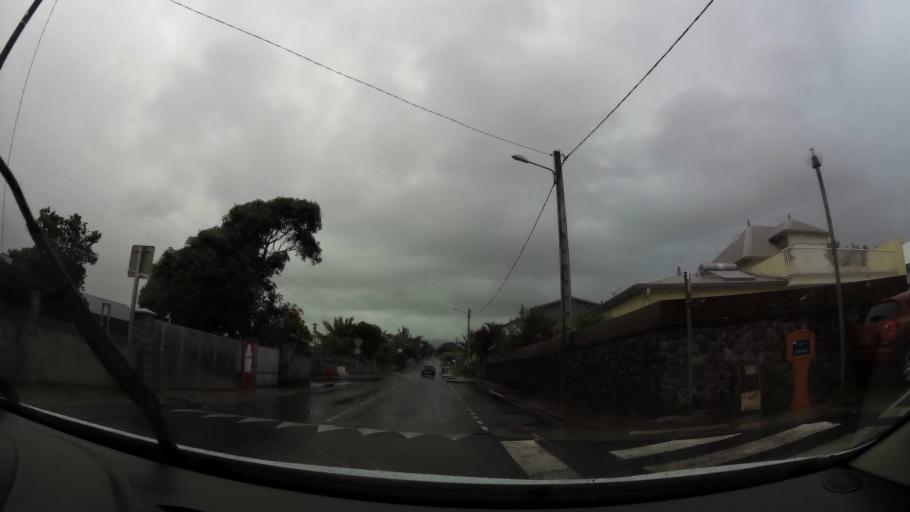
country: RE
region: Reunion
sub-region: Reunion
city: Saint-Benoit
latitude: -21.0197
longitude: 55.7013
